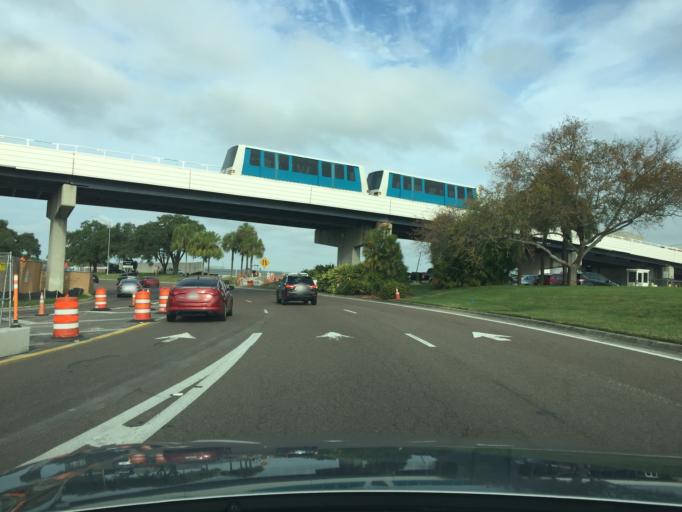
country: US
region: Florida
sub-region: Hillsborough County
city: Egypt Lake-Leto
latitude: 27.9812
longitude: -82.5328
